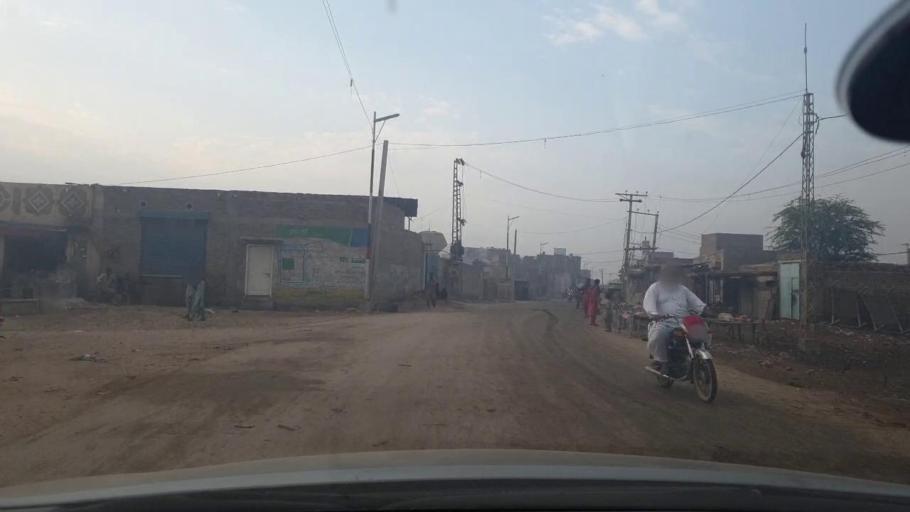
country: PK
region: Sindh
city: Jacobabad
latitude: 28.2816
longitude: 68.4256
